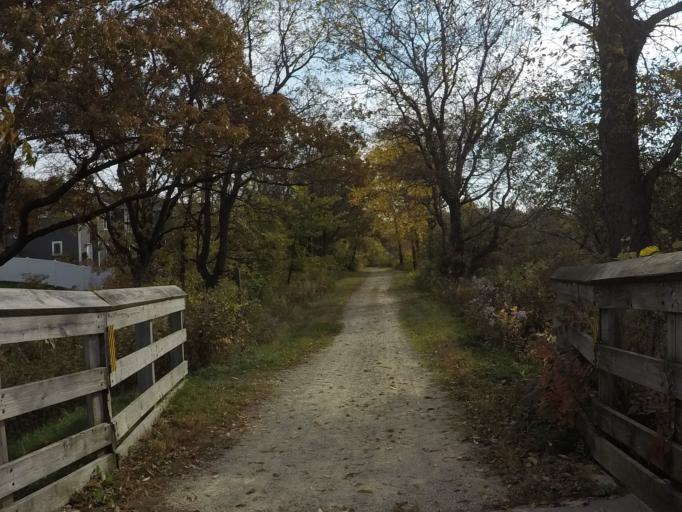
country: US
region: Wisconsin
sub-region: Iowa County
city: Barneveld
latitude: 43.0138
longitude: -89.8200
